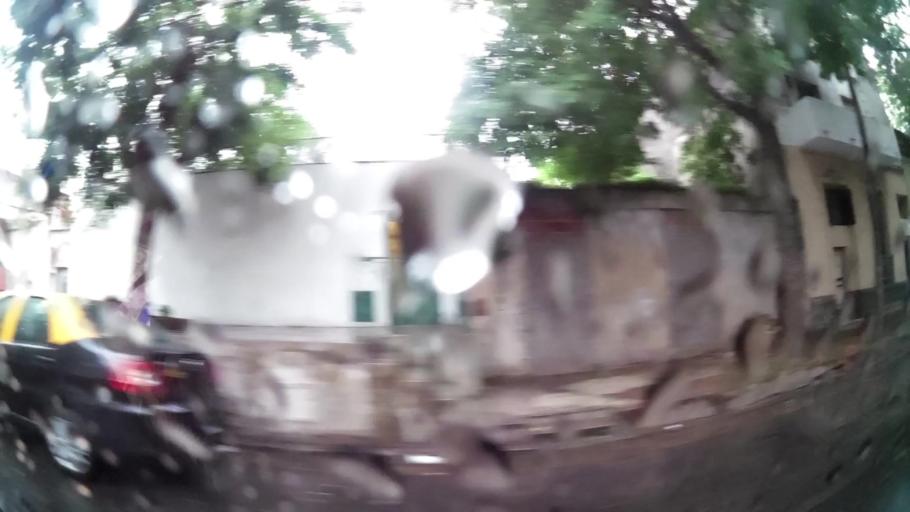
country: AR
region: Buenos Aires
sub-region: Partido de Avellaneda
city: Avellaneda
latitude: -34.6456
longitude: -58.3653
